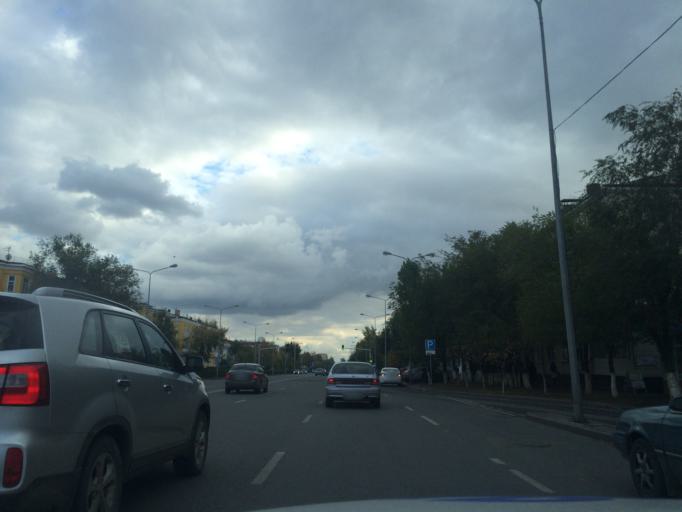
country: KZ
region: Astana Qalasy
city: Astana
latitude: 51.1848
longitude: 71.4084
